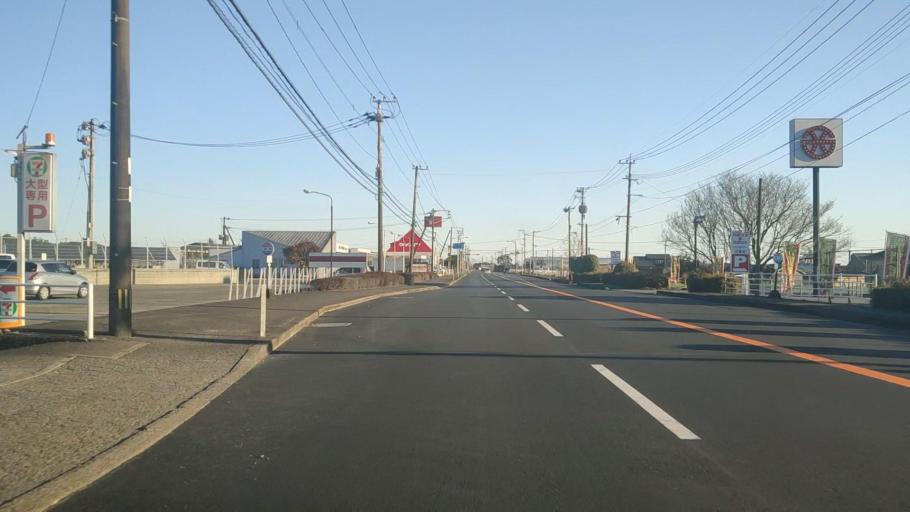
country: JP
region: Miyazaki
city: Takanabe
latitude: 32.2263
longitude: 131.5451
